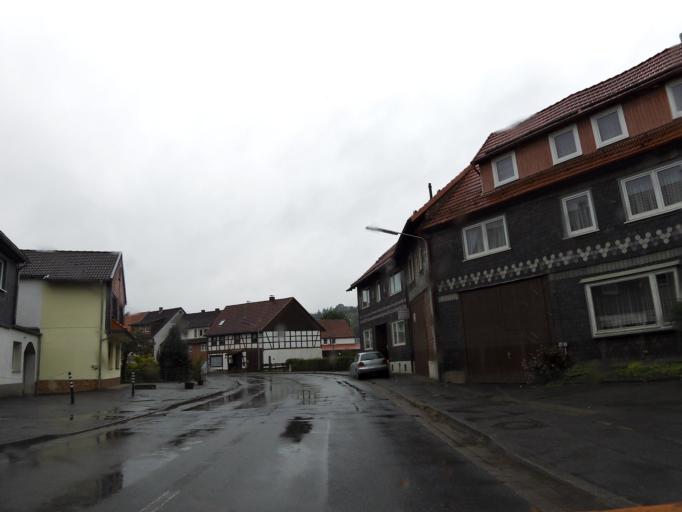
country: DE
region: Lower Saxony
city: Herzberg am Harz
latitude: 51.6275
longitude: 10.3854
